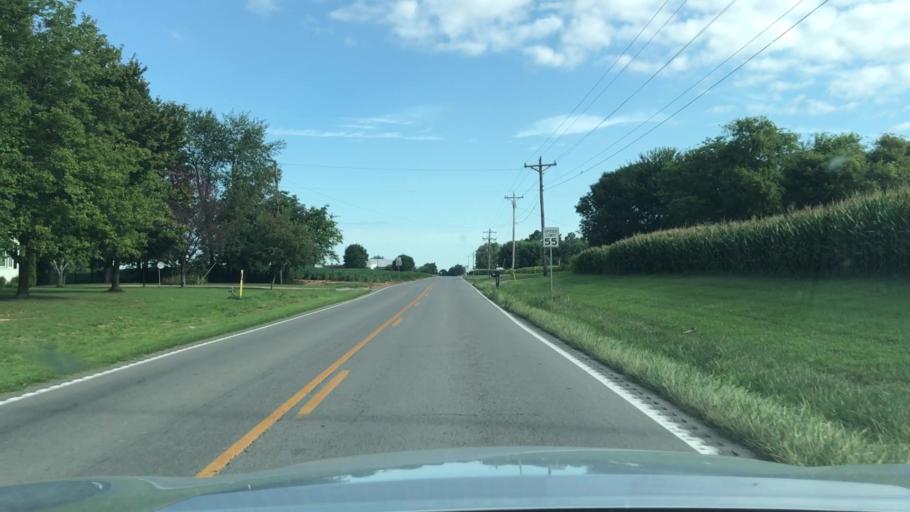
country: US
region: Kentucky
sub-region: Todd County
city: Elkton
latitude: 36.8676
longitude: -87.1631
